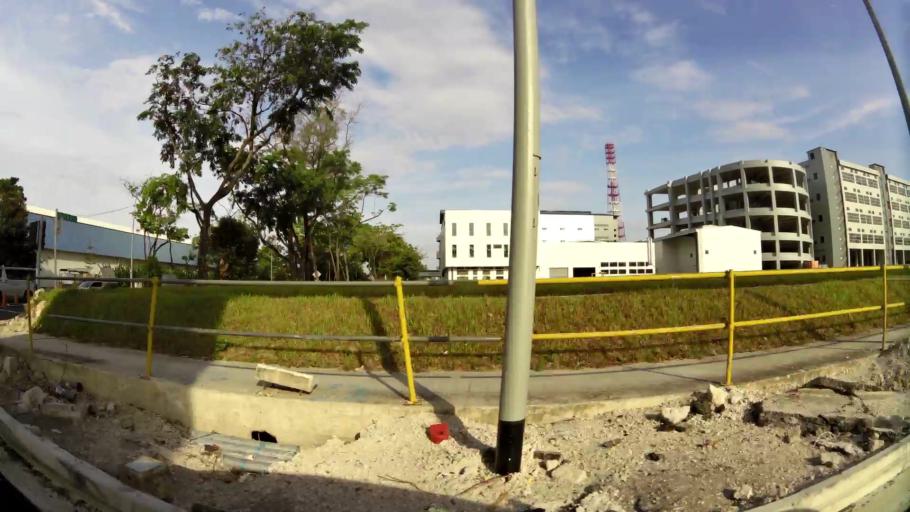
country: MY
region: Johor
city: Johor Bahru
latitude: 1.3169
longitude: 103.6576
